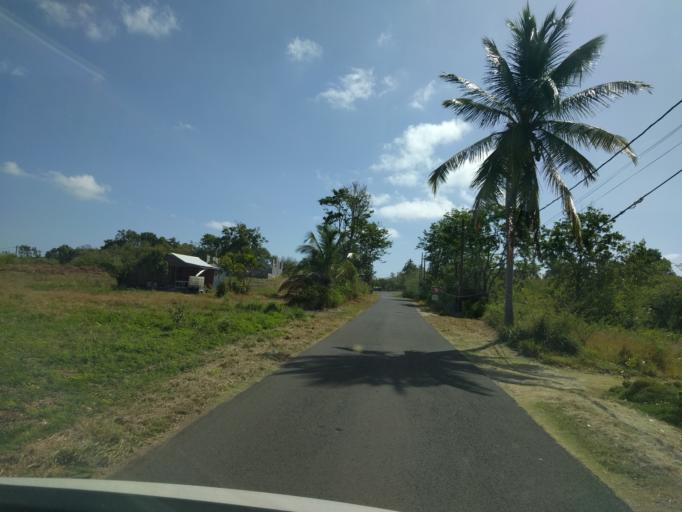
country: GP
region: Guadeloupe
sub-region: Guadeloupe
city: Grand-Bourg
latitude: 15.9791
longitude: -61.2446
